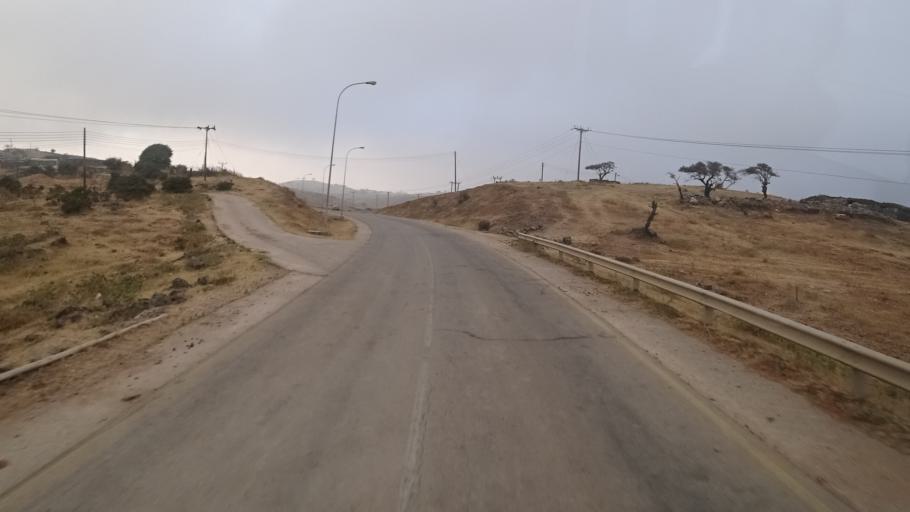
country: OM
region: Zufar
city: Salalah
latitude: 17.1307
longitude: 53.9769
